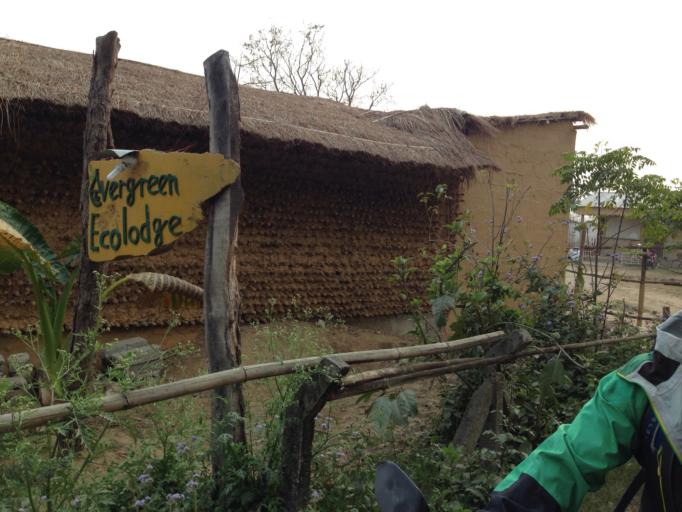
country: NP
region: Central Region
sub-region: Narayani Zone
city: Bharatpur
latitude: 27.5791
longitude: 84.4927
